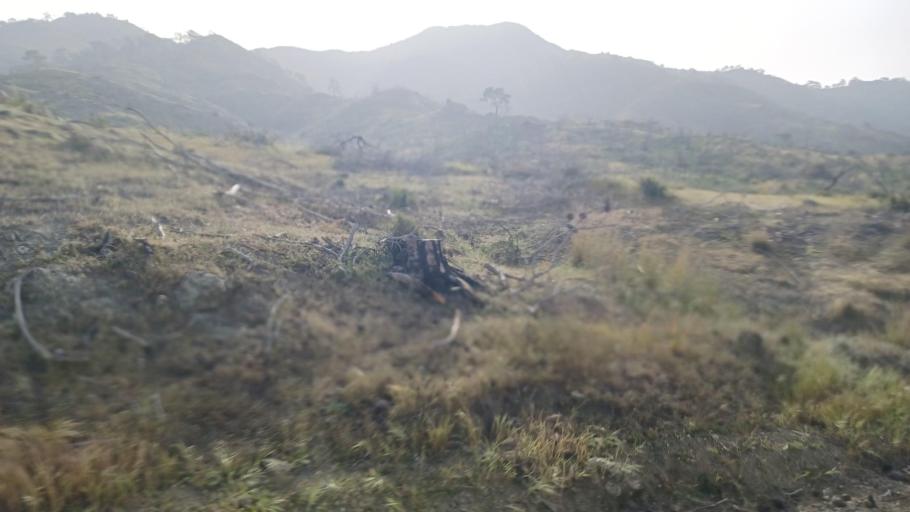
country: CY
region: Pafos
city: Polis
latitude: 34.9949
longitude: 32.3324
